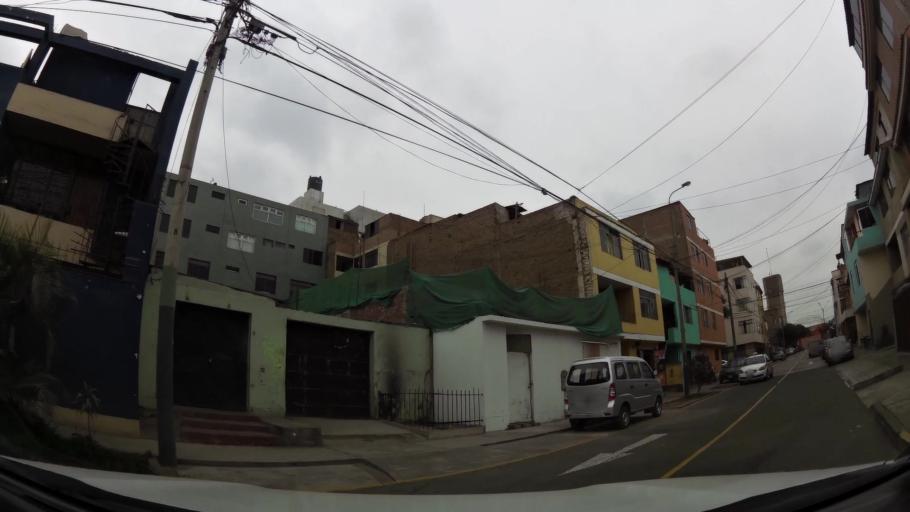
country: PE
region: Lima
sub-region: Lima
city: Surco
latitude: -12.1077
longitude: -77.0092
